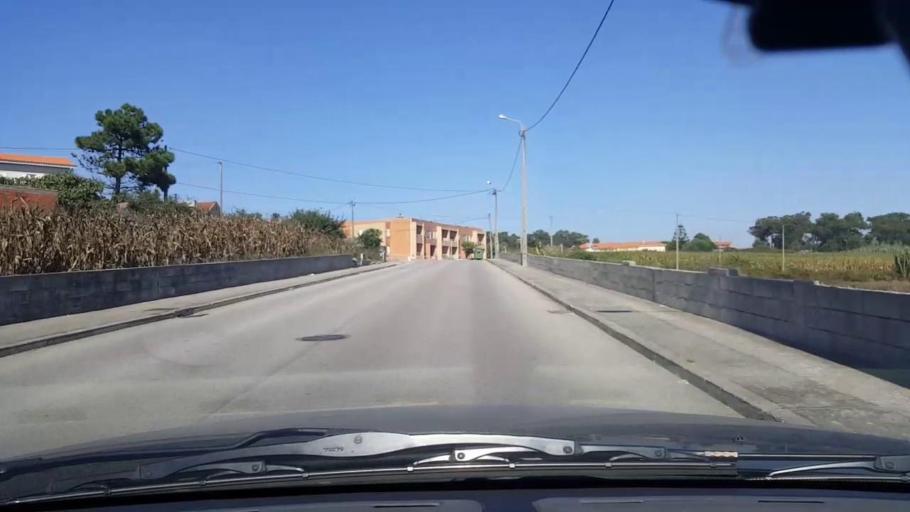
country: PT
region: Porto
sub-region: Matosinhos
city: Lavra
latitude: 41.2946
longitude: -8.7327
